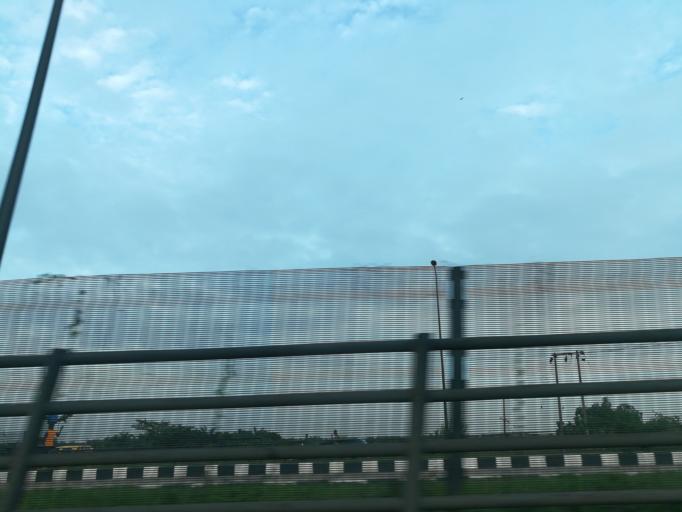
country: NG
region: Lagos
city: Ebute Ikorodu
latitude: 6.6117
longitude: 3.4411
